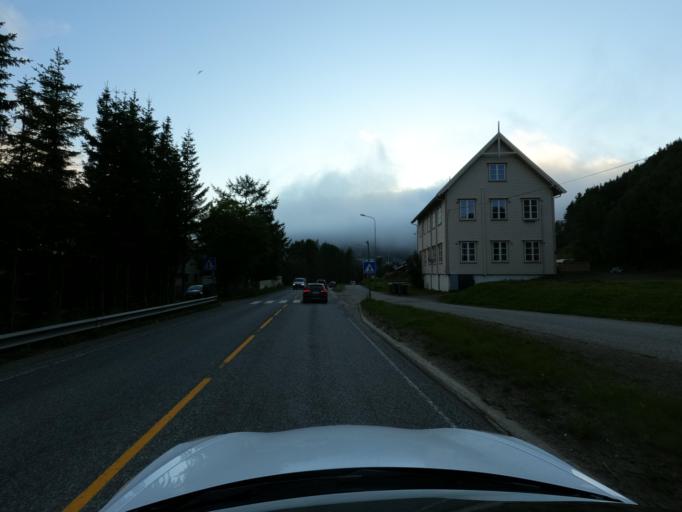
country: NO
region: Troms
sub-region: Harstad
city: Harstad
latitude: 68.8058
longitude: 16.5156
